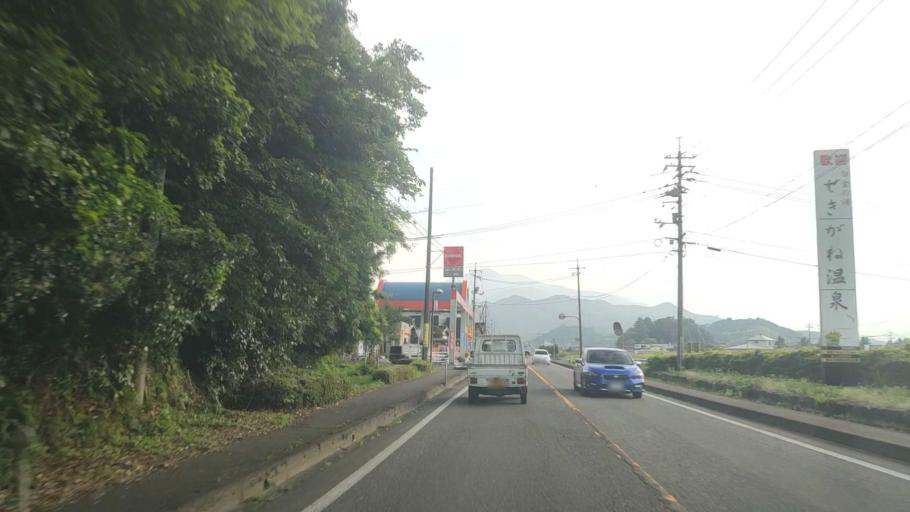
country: JP
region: Tottori
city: Kurayoshi
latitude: 35.3681
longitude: 133.7628
